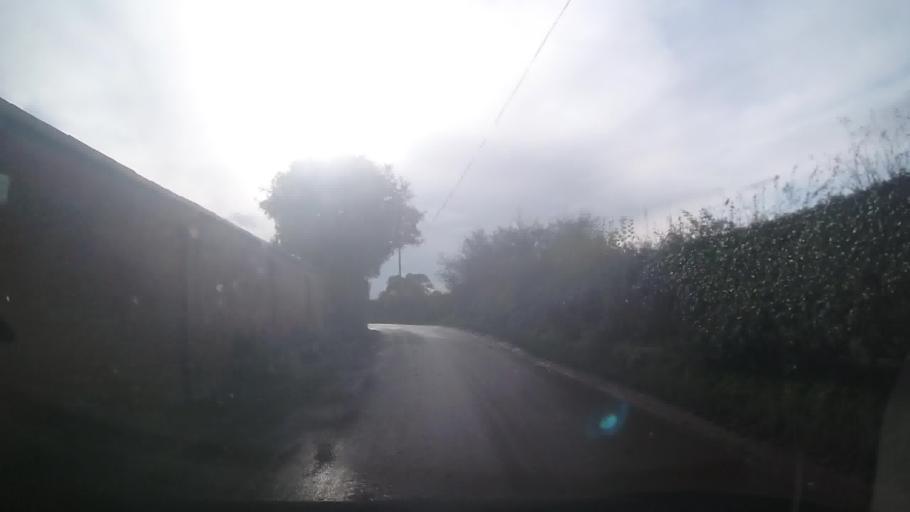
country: GB
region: England
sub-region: Shropshire
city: Whitchurch
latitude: 52.9526
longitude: -2.6980
